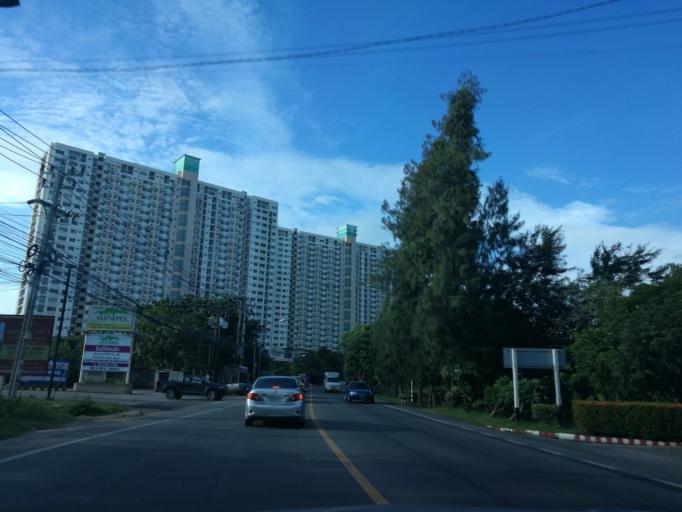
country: TH
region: Bangkok
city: Bang Na
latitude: 13.6700
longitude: 100.6443
